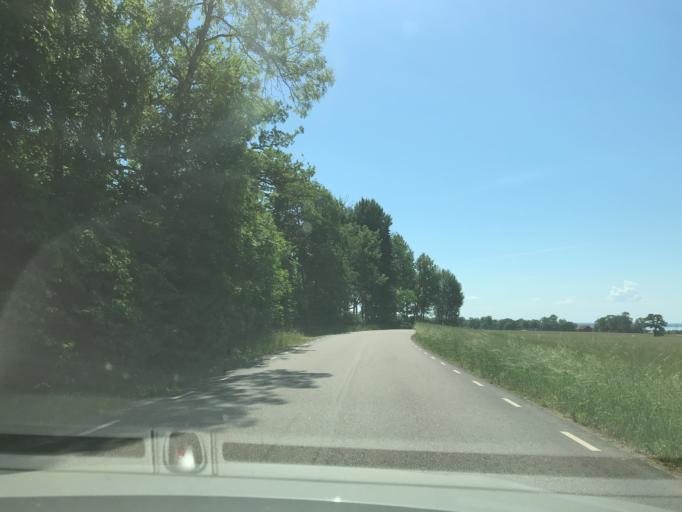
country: SE
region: Vaestra Goetaland
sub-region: Gotene Kommun
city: Kallby
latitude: 58.5527
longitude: 13.3452
